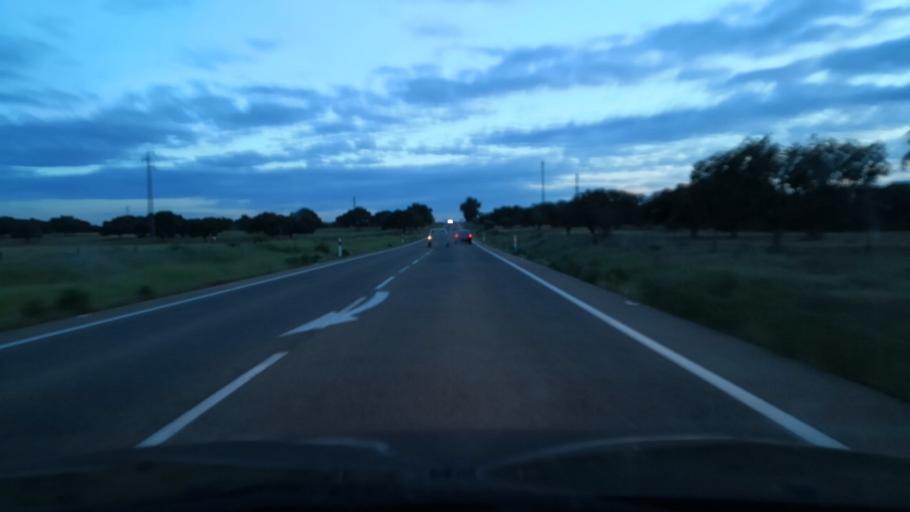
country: ES
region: Extremadura
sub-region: Provincia de Badajoz
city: Badajoz
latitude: 38.9510
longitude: -6.9115
